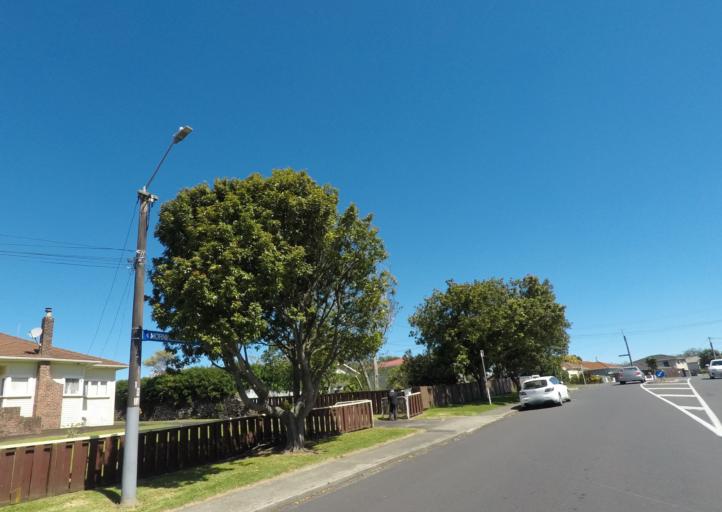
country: NZ
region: Auckland
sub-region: Auckland
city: Auckland
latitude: -36.8794
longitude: 174.7347
